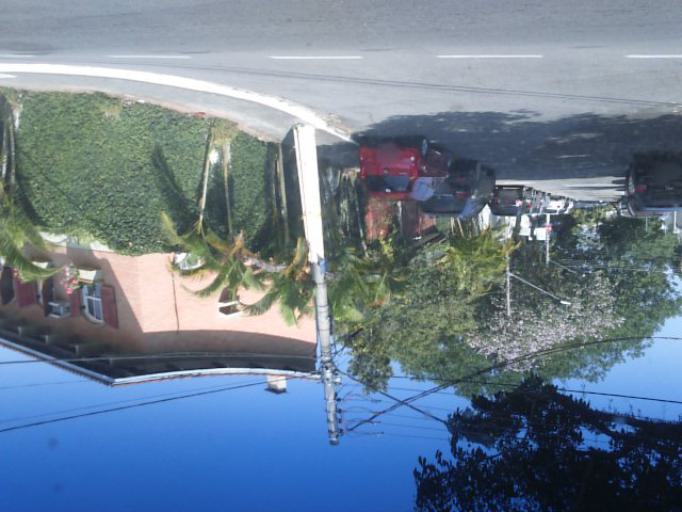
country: BR
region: Sao Paulo
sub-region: Sao Jose Dos Campos
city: Sao Jose dos Campos
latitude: -23.1928
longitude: -45.9037
